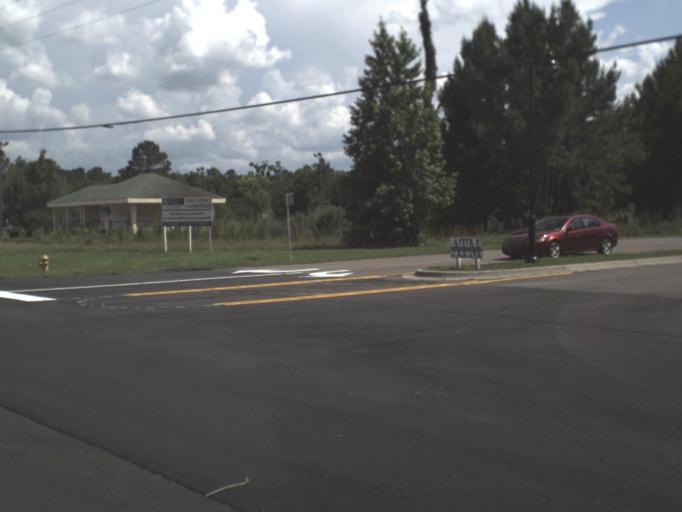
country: US
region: Florida
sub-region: Alachua County
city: Alachua
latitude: 29.7584
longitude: -82.4016
